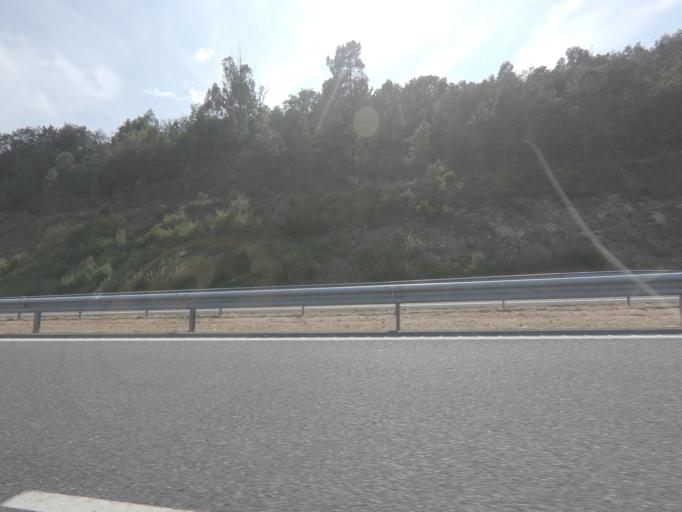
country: ES
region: Galicia
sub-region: Provincia de Ourense
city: Cenlle
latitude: 42.3243
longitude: -8.0770
